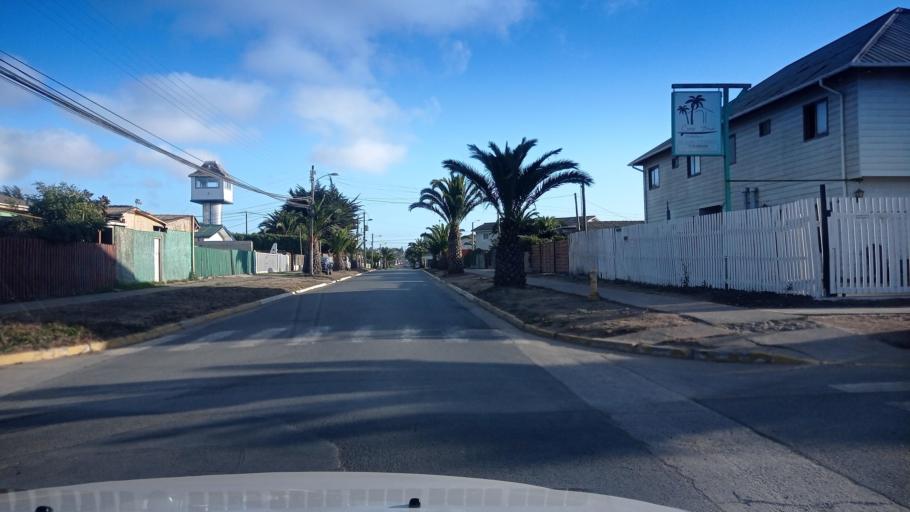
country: CL
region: O'Higgins
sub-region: Provincia de Colchagua
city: Santa Cruz
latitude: -34.3870
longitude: -72.0114
